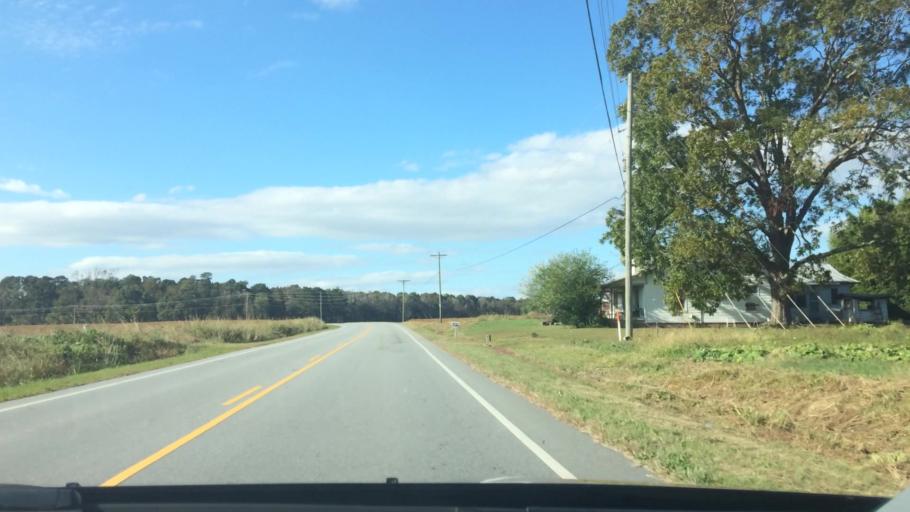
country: US
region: North Carolina
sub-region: Greene County
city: Maury
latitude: 35.4825
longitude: -77.5643
